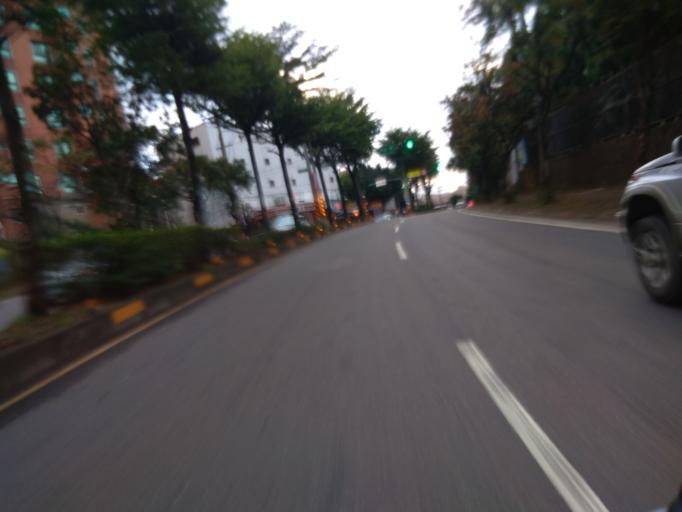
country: TW
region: Taiwan
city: Daxi
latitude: 24.9226
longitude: 121.1783
